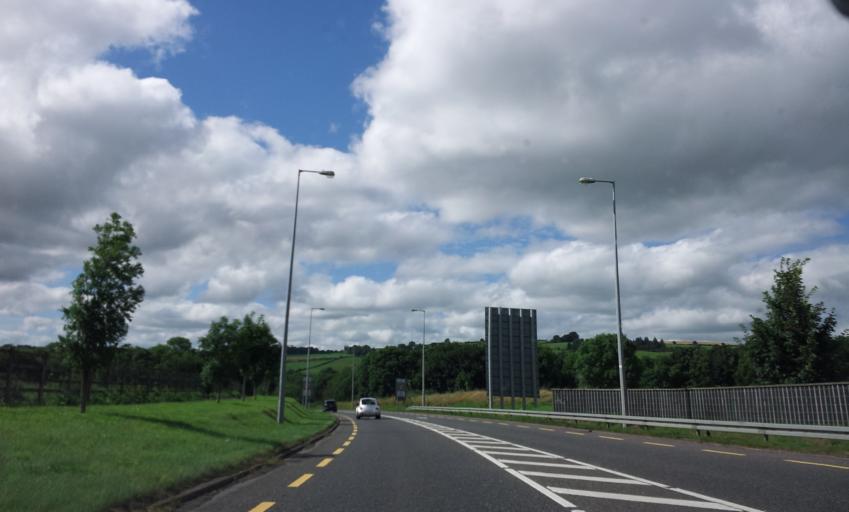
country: IE
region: Munster
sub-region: County Cork
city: Killumney
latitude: 51.8789
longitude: -8.6495
